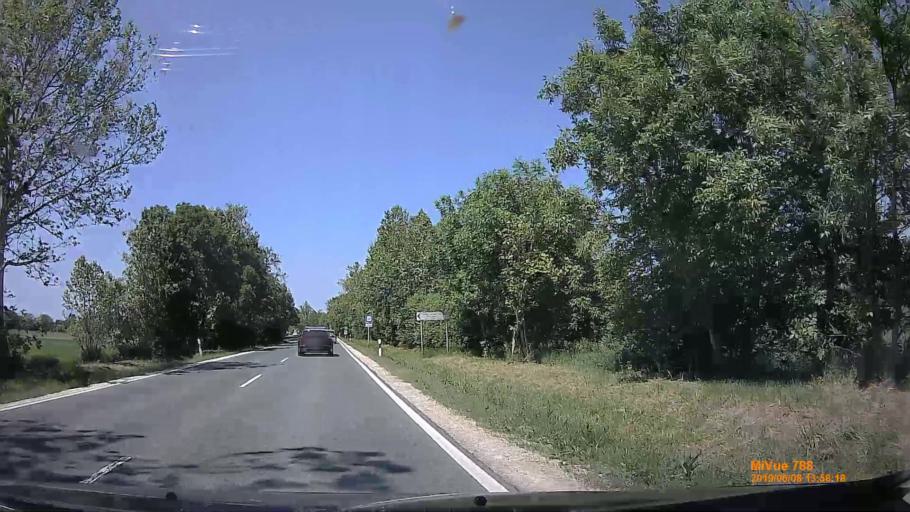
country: HU
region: Vas
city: Sarvar
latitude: 47.3754
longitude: 16.8842
